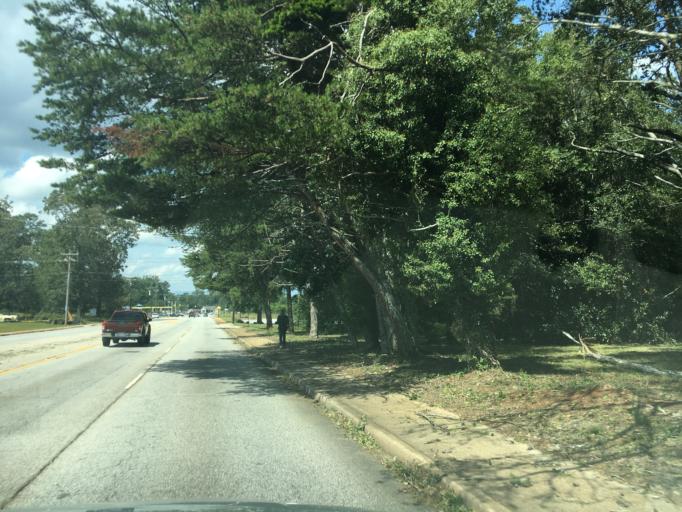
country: US
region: South Carolina
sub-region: Greenville County
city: Berea
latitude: 34.8881
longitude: -82.4640
